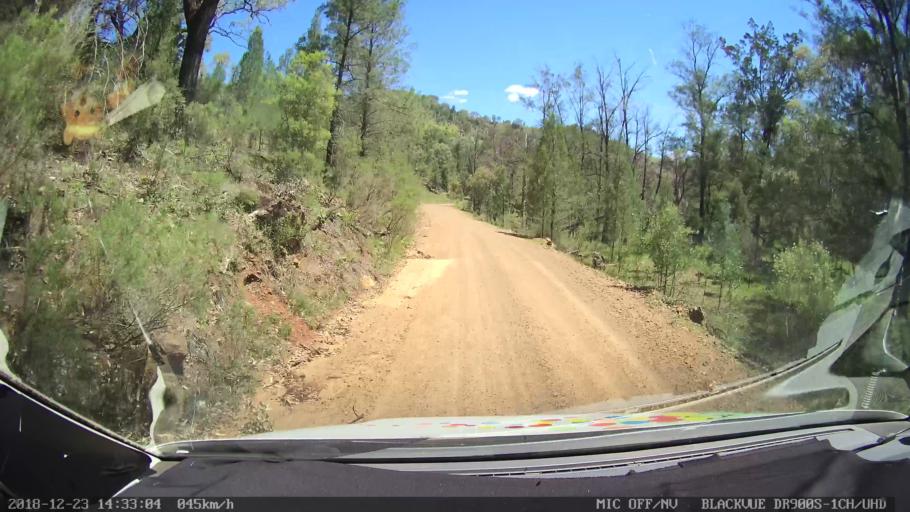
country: AU
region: New South Wales
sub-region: Tamworth Municipality
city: Manilla
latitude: -30.6060
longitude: 150.9151
